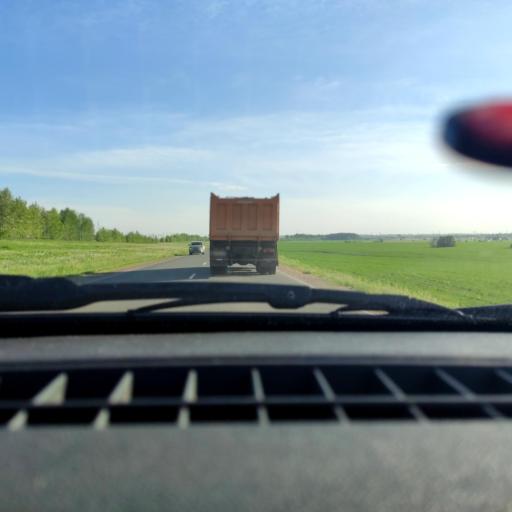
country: RU
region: Bashkortostan
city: Avdon
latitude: 54.4476
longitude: 55.8444
